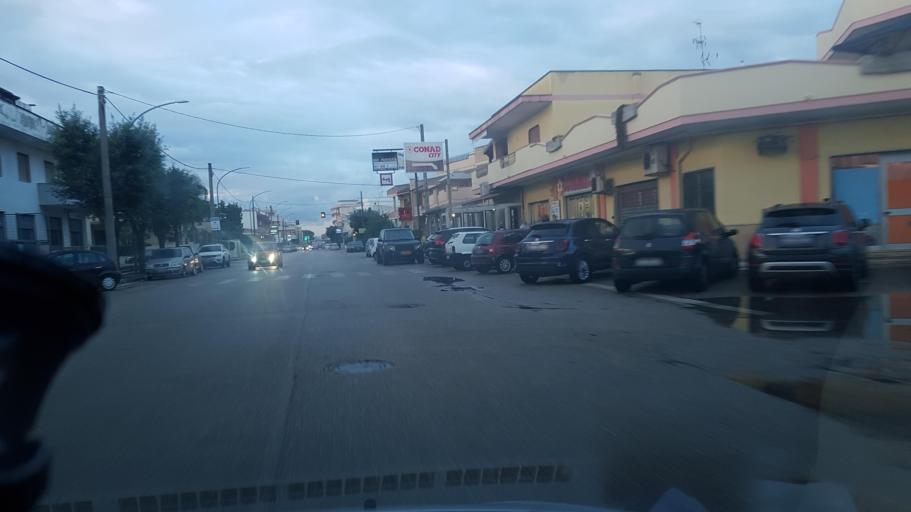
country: IT
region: Apulia
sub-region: Provincia di Lecce
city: Surbo
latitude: 40.3869
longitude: 18.1339
